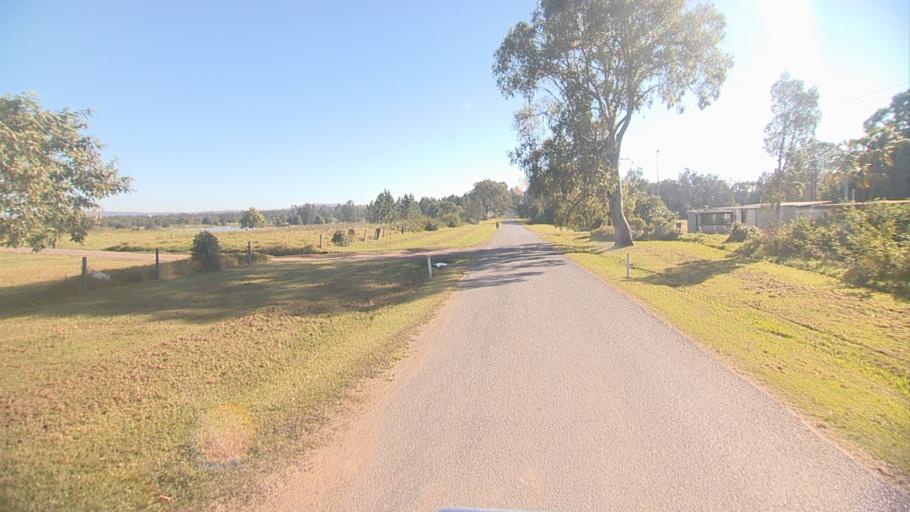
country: AU
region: Queensland
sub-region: Gold Coast
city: Yatala
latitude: -27.6896
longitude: 153.2605
